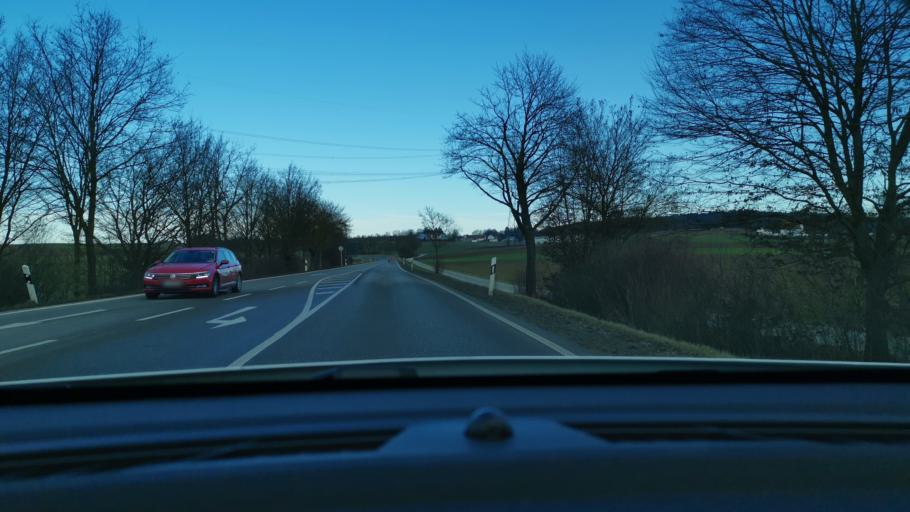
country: DE
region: Bavaria
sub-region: Swabia
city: Petersdorf
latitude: 48.5124
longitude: 11.0188
